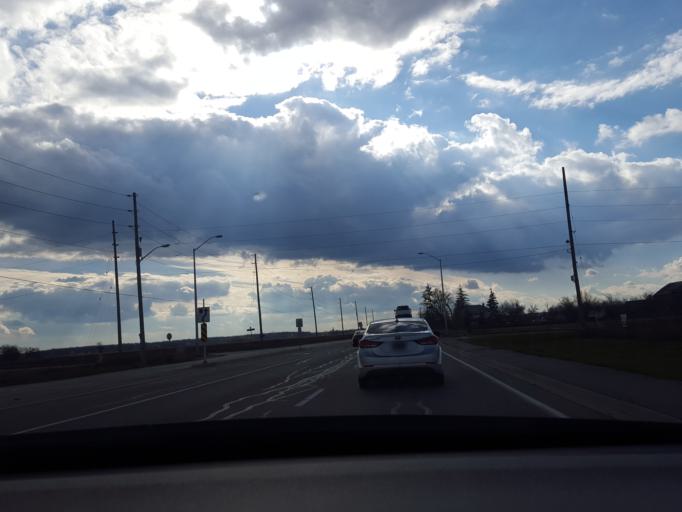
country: CA
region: Ontario
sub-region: Halton
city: Milton
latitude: 43.5656
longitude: -79.7968
